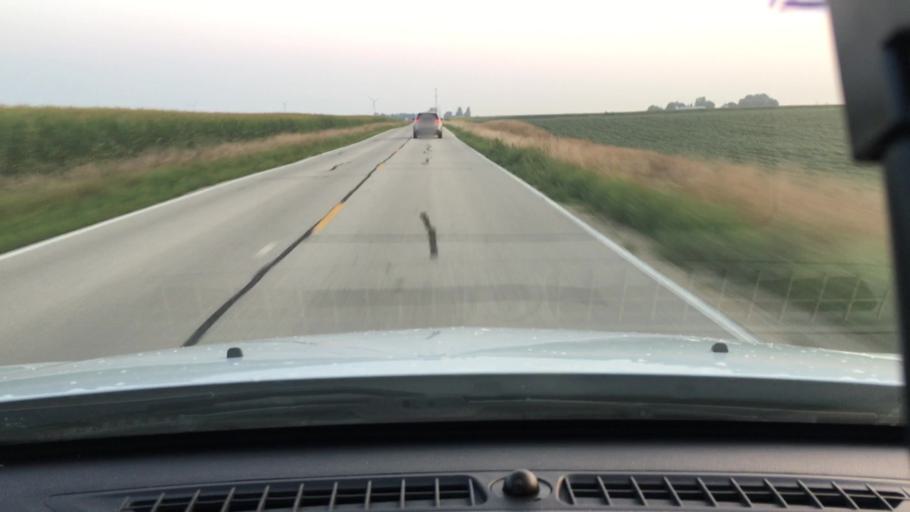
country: US
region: Illinois
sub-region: DeKalb County
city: Malta
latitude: 41.8526
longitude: -88.8478
